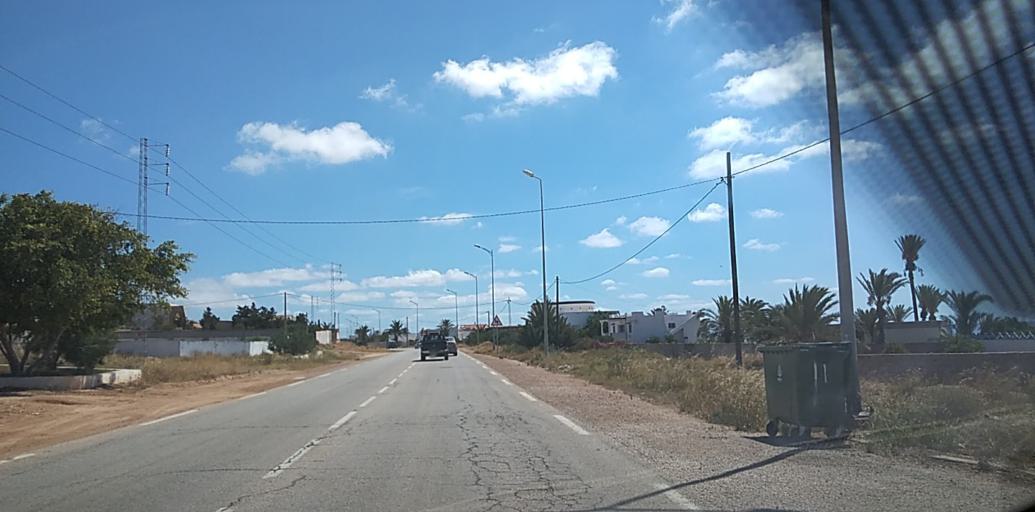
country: TN
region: Safaqis
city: Al Qarmadah
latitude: 34.6734
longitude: 11.1453
